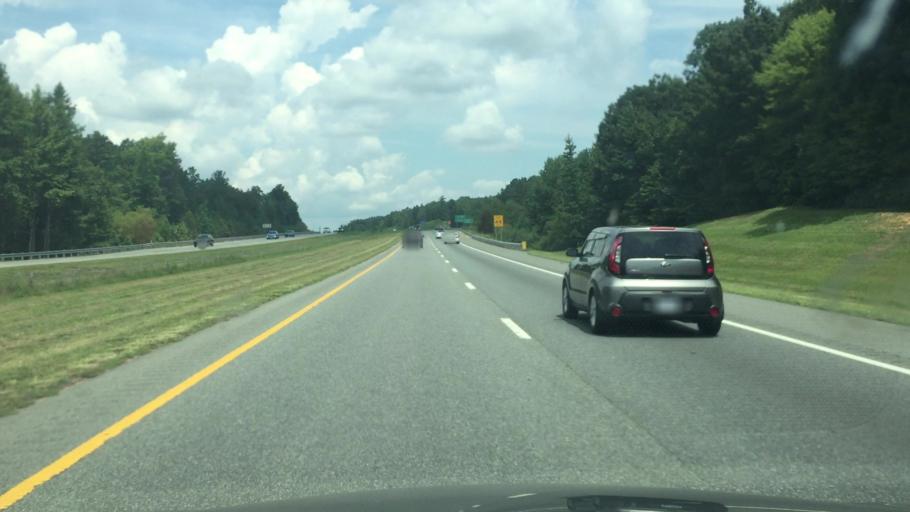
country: US
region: North Carolina
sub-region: Montgomery County
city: Biscoe
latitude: 35.5093
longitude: -79.7811
